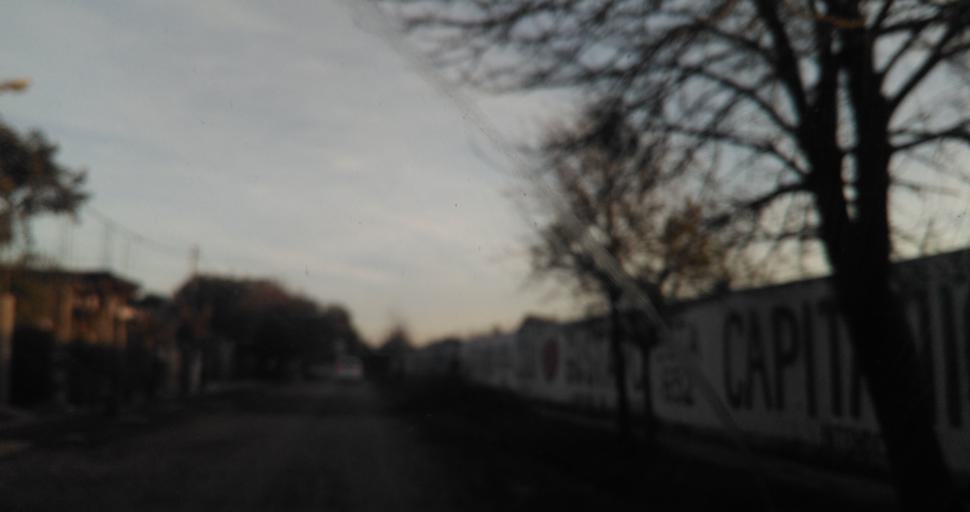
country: AR
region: Chaco
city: Resistencia
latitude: -27.4680
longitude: -59.0071
